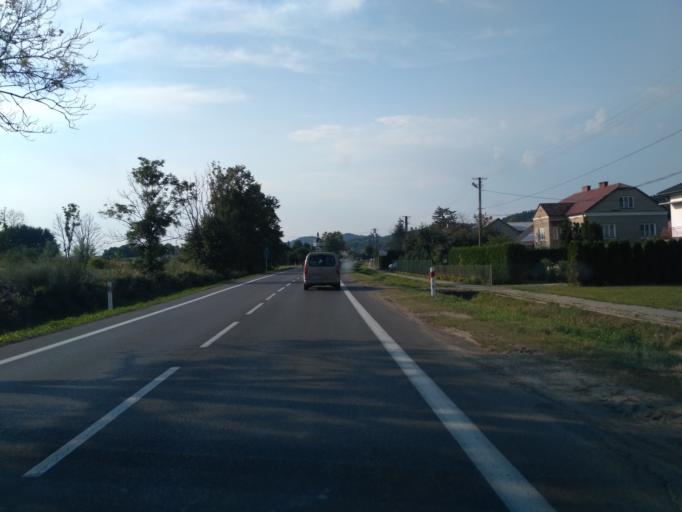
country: PL
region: Subcarpathian Voivodeship
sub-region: Powiat brzozowski
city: Stara Wies
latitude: 49.7148
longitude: 22.0123
